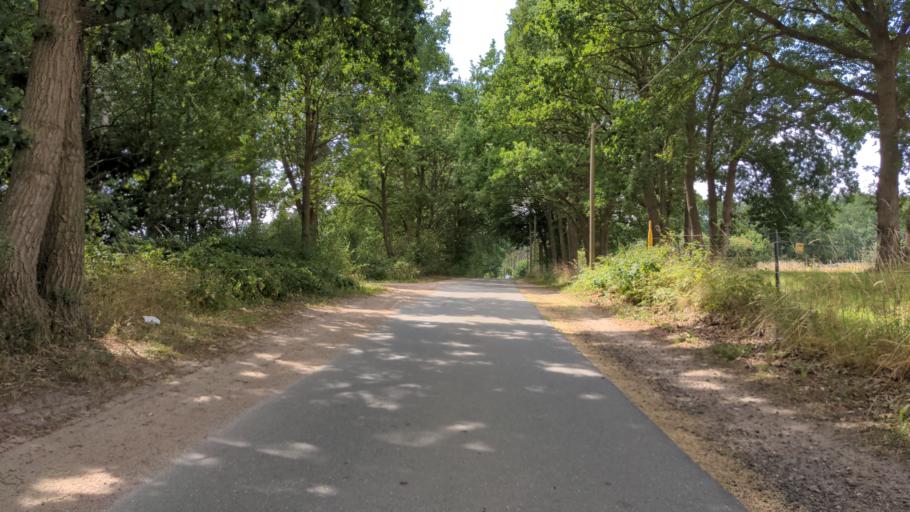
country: DE
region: Schleswig-Holstein
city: Gross Gronau
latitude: 53.8500
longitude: 10.7937
